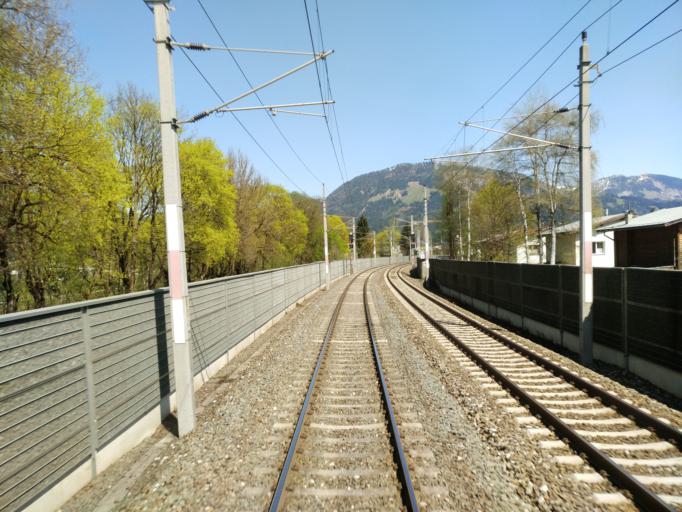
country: AT
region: Tyrol
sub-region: Politischer Bezirk Kitzbuhel
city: Sankt Johann in Tirol
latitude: 47.5193
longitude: 12.4196
